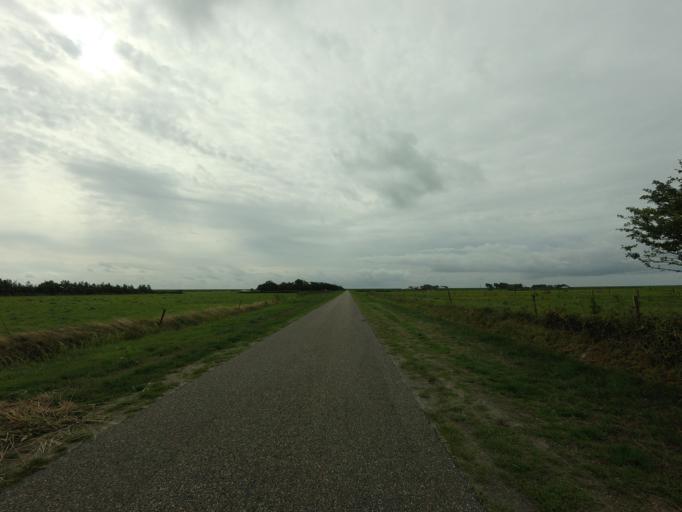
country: NL
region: Friesland
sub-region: Gemeente Ameland
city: Nes
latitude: 53.4400
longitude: 5.7076
